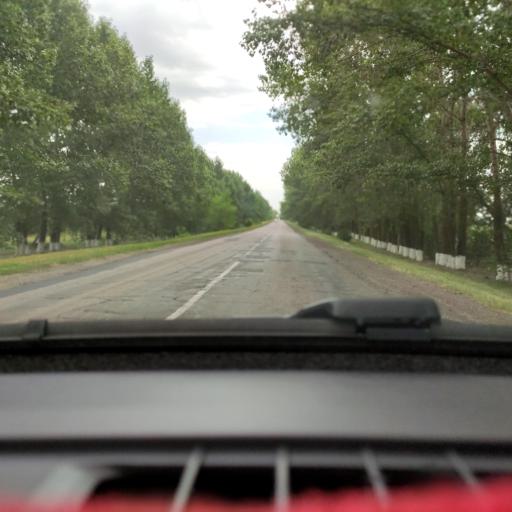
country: RU
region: Voronezj
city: Davydovka
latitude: 51.2473
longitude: 39.5480
